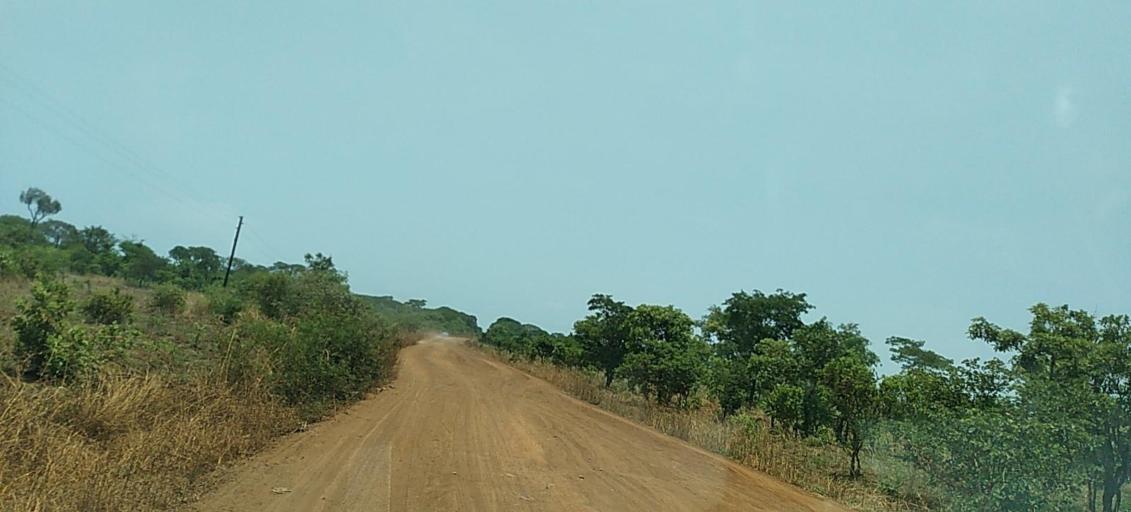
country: ZM
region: Copperbelt
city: Mpongwe
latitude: -13.6930
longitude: 27.8629
